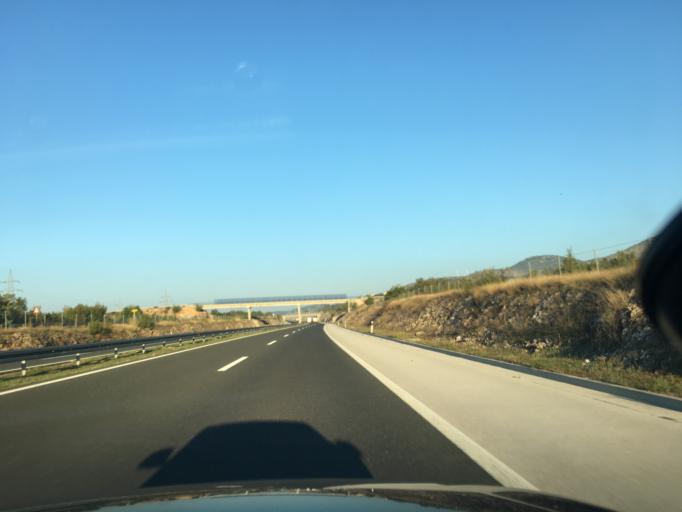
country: HR
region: Sibensko-Kniniska
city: Drnis
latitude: 43.6807
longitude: 16.1345
